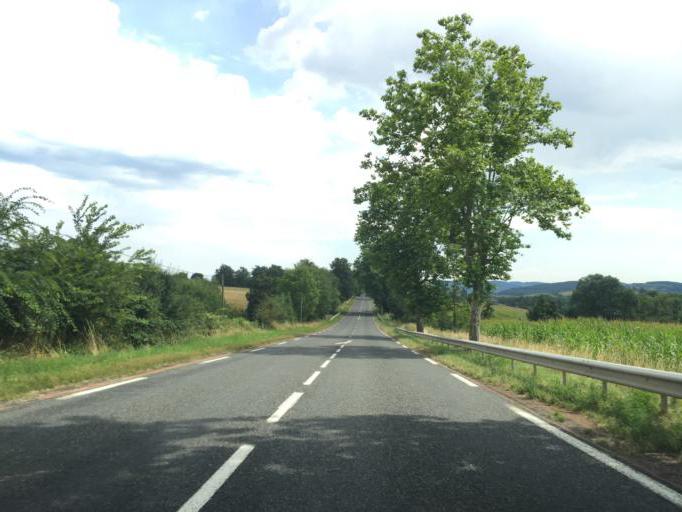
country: FR
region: Rhone-Alpes
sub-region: Departement du Rhone
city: Saint-Romain-de-Popey
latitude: 45.8738
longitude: 4.5368
